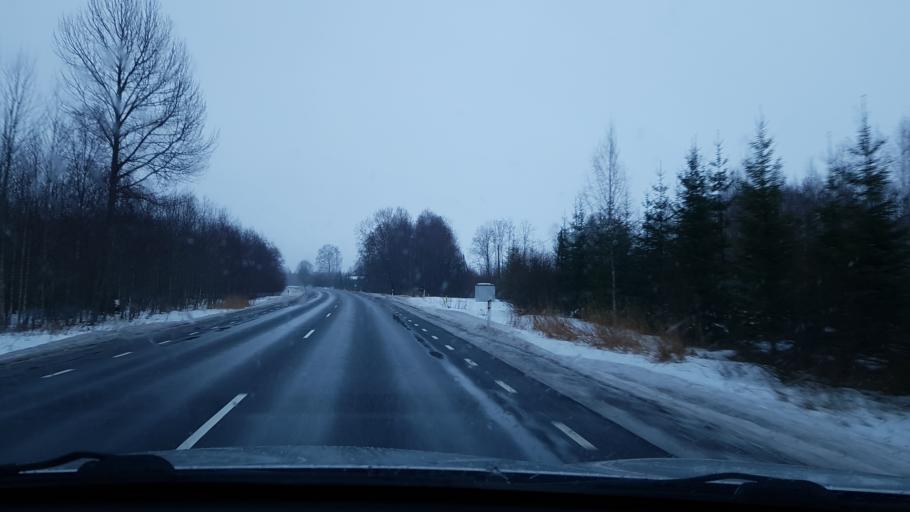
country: EE
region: Jaervamaa
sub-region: Tueri vald
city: Sarevere
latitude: 58.8007
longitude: 25.2351
